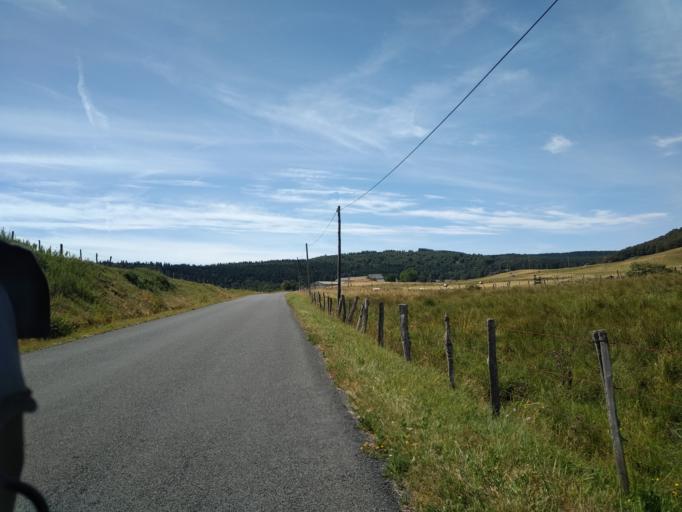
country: FR
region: Midi-Pyrenees
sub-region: Departement de l'Aveyron
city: Laguiole
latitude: 44.6818
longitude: 2.9946
